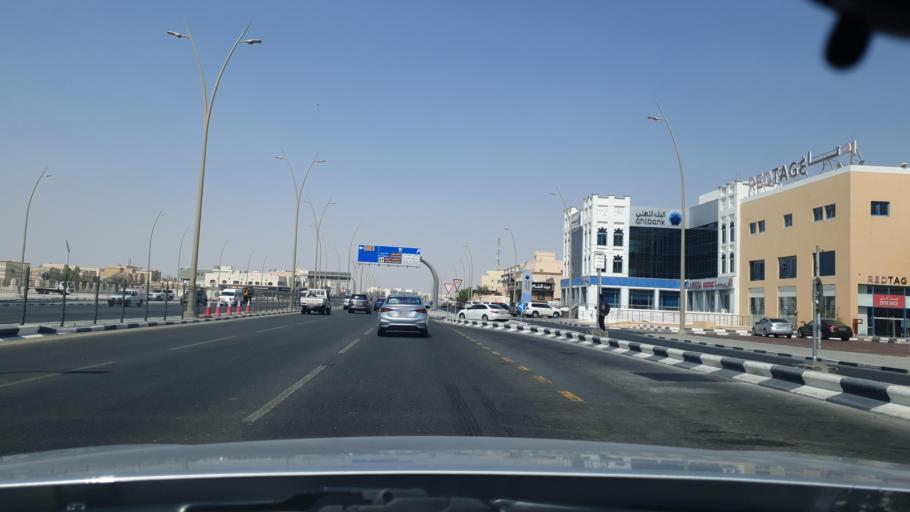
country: QA
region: Al Khawr
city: Al Khawr
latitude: 25.6763
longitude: 51.5001
